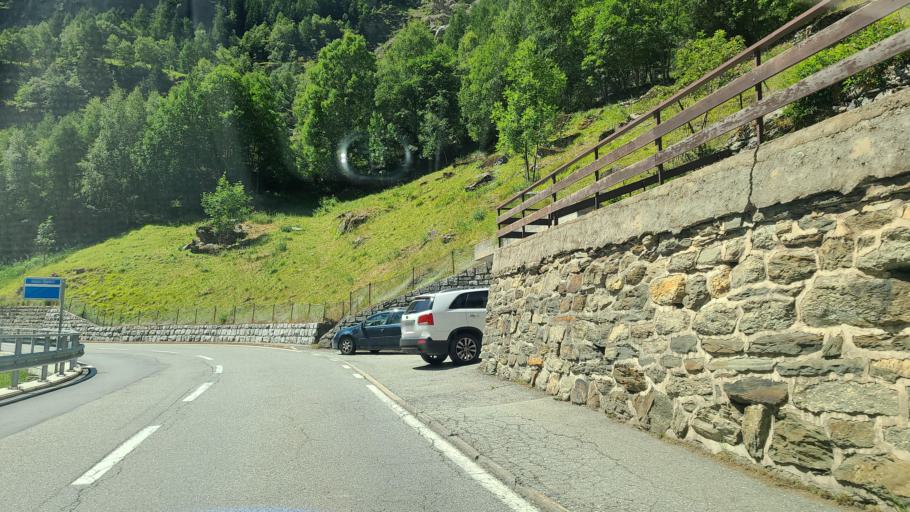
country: CH
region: Valais
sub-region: Visp District
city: Stalden
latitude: 46.1950
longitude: 7.8965
